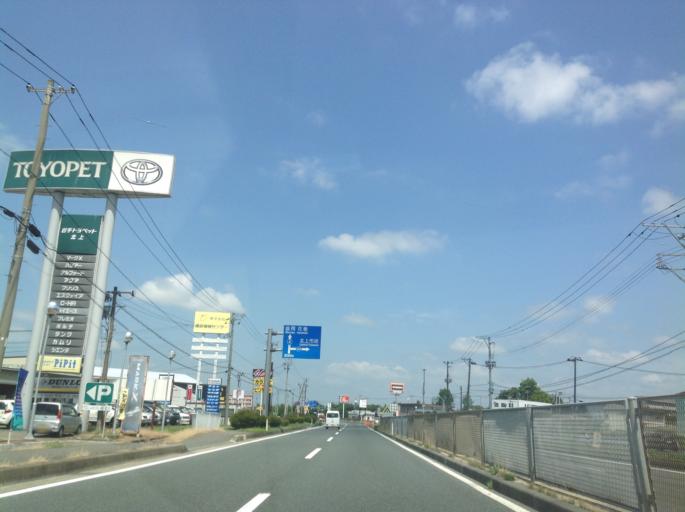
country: JP
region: Iwate
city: Kitakami
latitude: 39.3096
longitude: 141.1113
